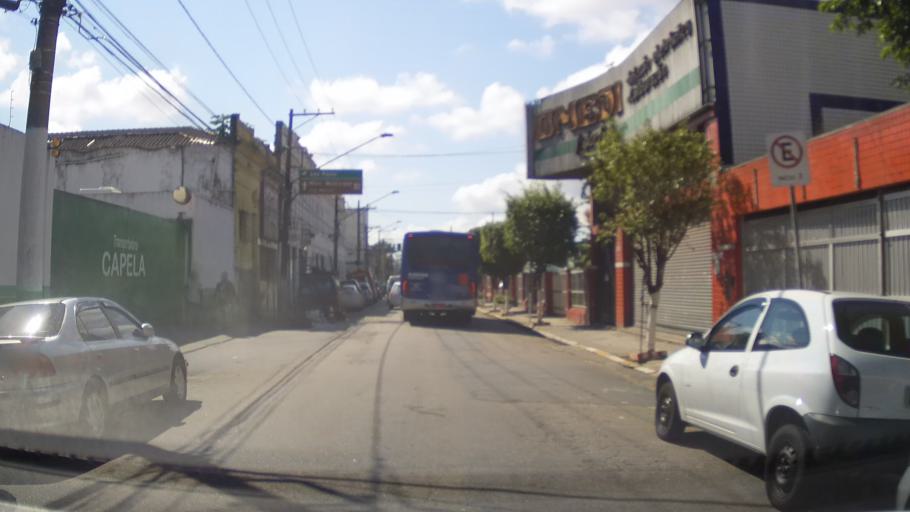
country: BR
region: Sao Paulo
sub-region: Santos
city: Santos
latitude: -23.9382
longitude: -46.3219
